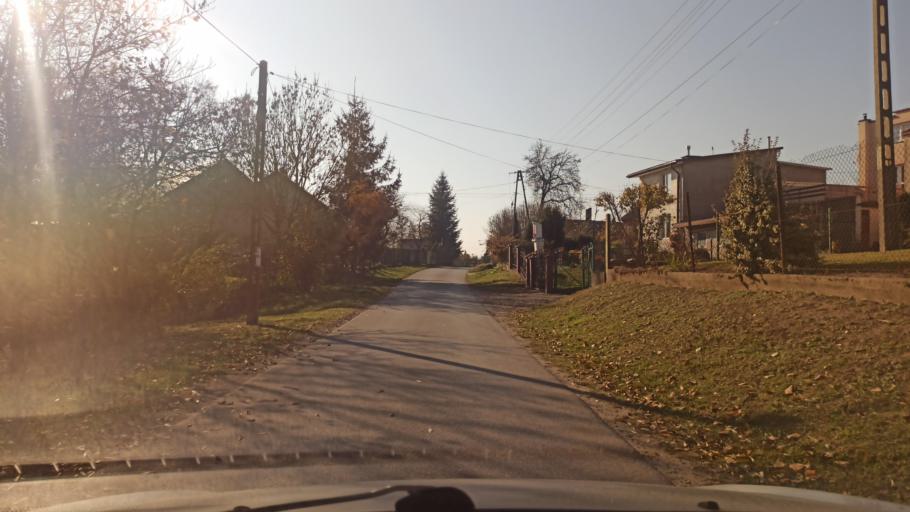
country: PL
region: Subcarpathian Voivodeship
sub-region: Powiat jaroslawski
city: Radymno
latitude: 49.9403
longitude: 22.8148
